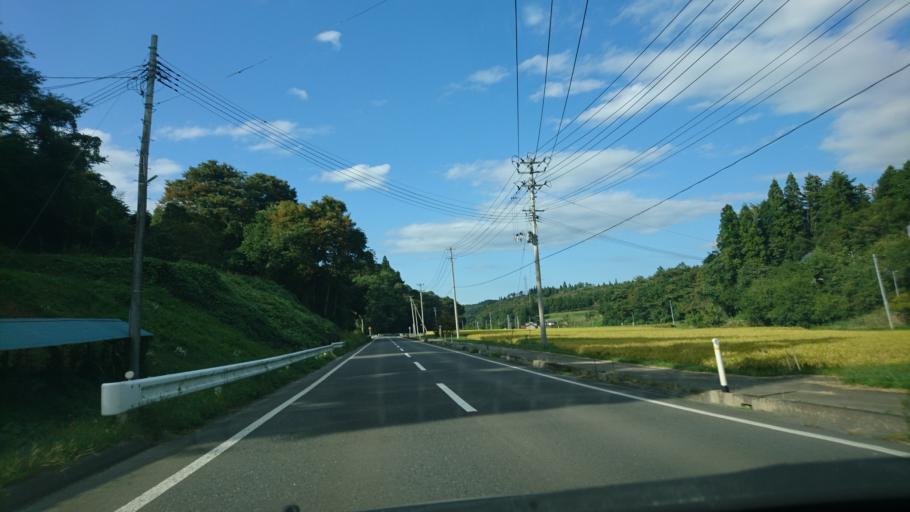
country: JP
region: Iwate
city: Ichinoseki
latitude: 38.8823
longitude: 141.3324
